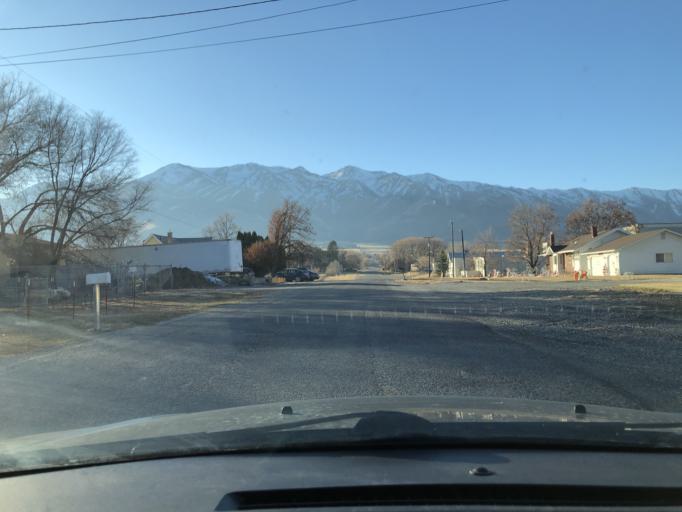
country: US
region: Utah
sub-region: Cache County
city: Wellsville
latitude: 41.6449
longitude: -111.9272
